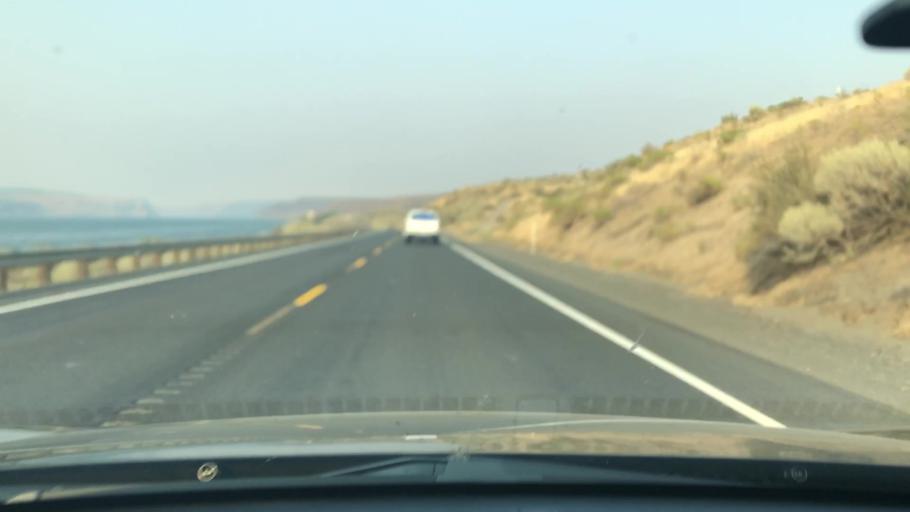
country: US
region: Oregon
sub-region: Umatilla County
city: Stanfield
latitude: 45.9223
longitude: -119.1169
